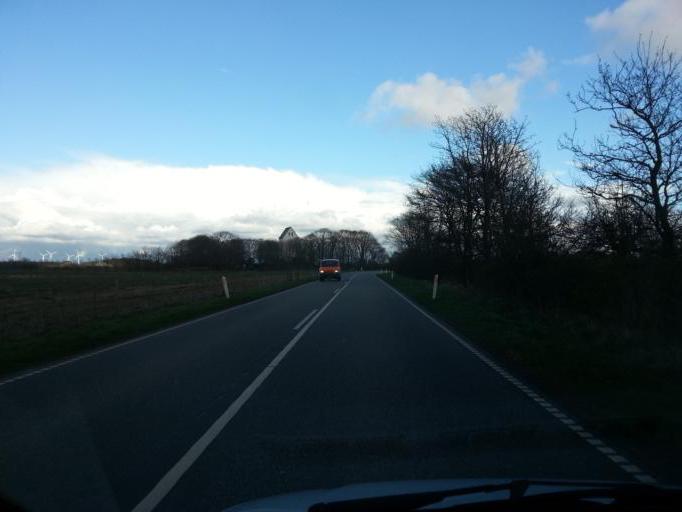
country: DK
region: Central Jutland
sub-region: Ringkobing-Skjern Kommune
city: Tarm
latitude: 55.8859
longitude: 8.5213
